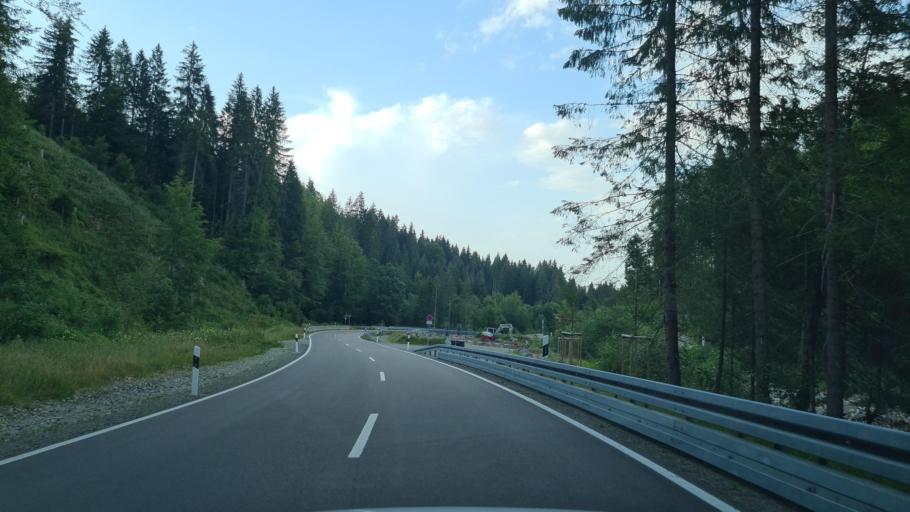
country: DE
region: Bavaria
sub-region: Swabia
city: Obermaiselstein
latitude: 47.4441
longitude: 10.2301
